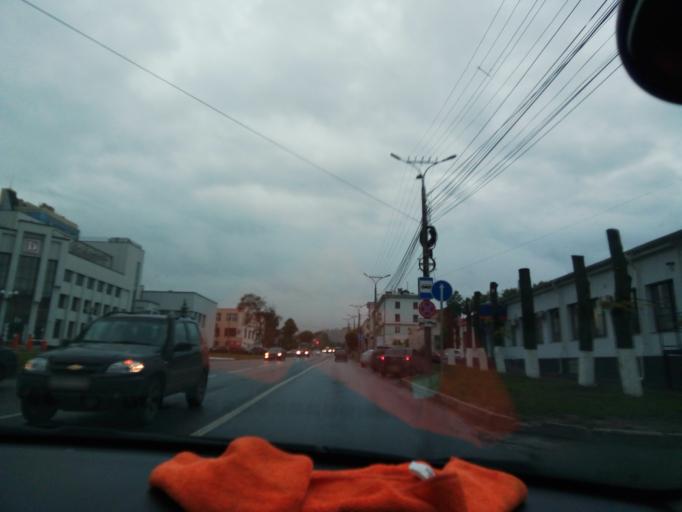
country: RU
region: Chuvashia
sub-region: Cheboksarskiy Rayon
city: Cheboksary
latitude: 56.1430
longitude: 47.2533
